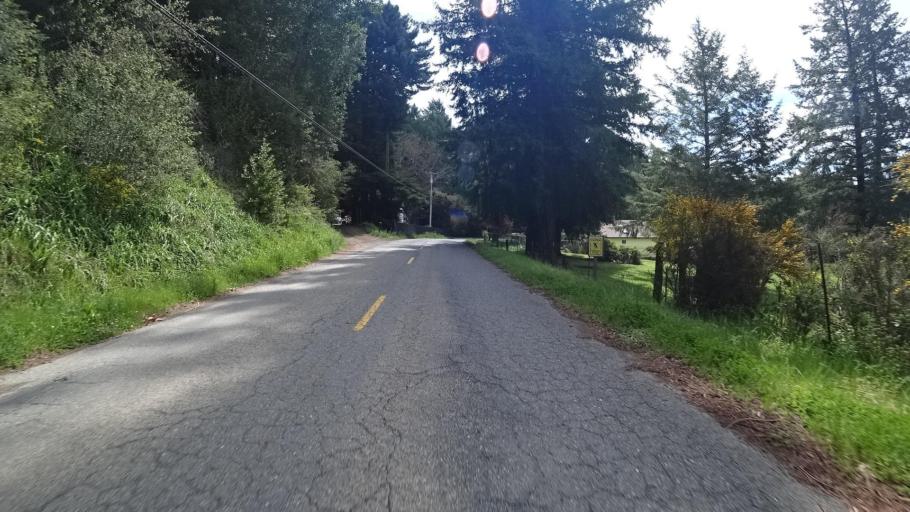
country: US
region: California
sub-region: Humboldt County
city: Redway
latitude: 40.0291
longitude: -123.9486
